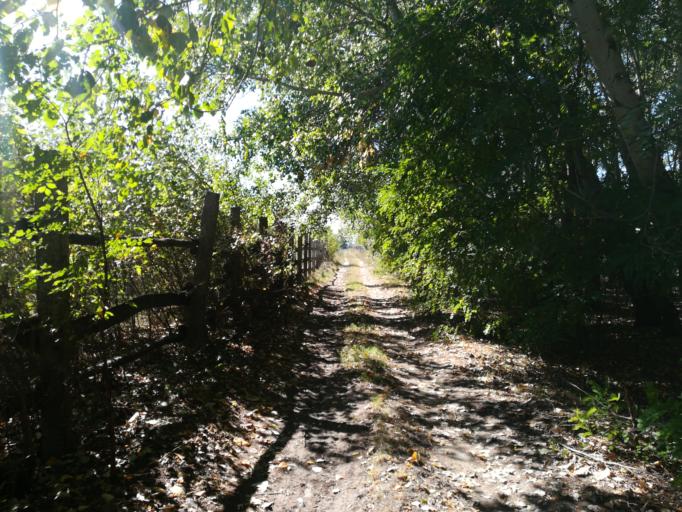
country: HU
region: Bacs-Kiskun
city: Tiszakecske
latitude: 46.9461
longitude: 20.0759
